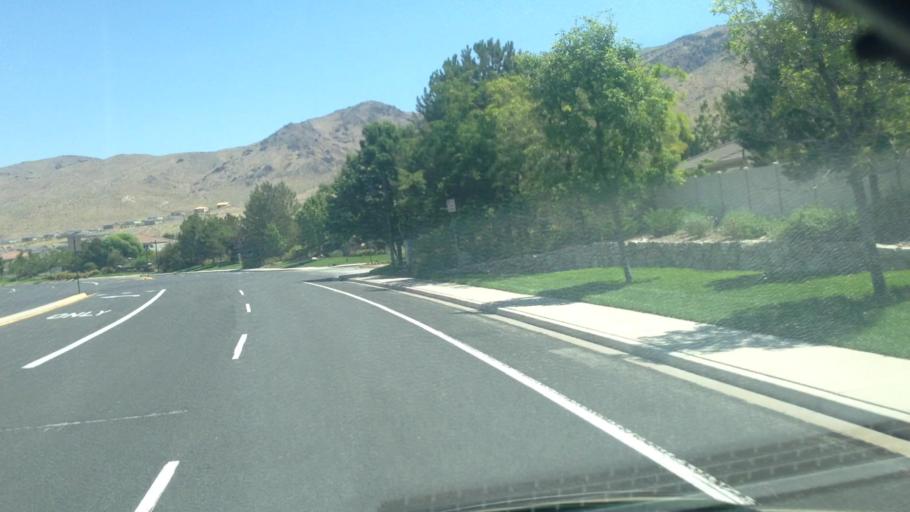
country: US
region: Nevada
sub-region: Washoe County
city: Sparks
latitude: 39.4181
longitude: -119.7204
